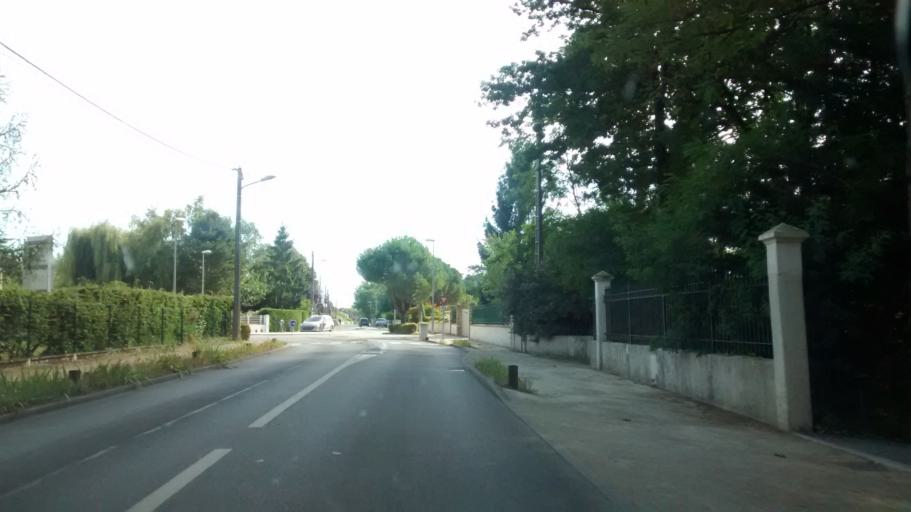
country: FR
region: Pays de la Loire
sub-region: Departement de la Loire-Atlantique
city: Pont-Saint-Martin
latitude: 47.1302
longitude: -1.6152
